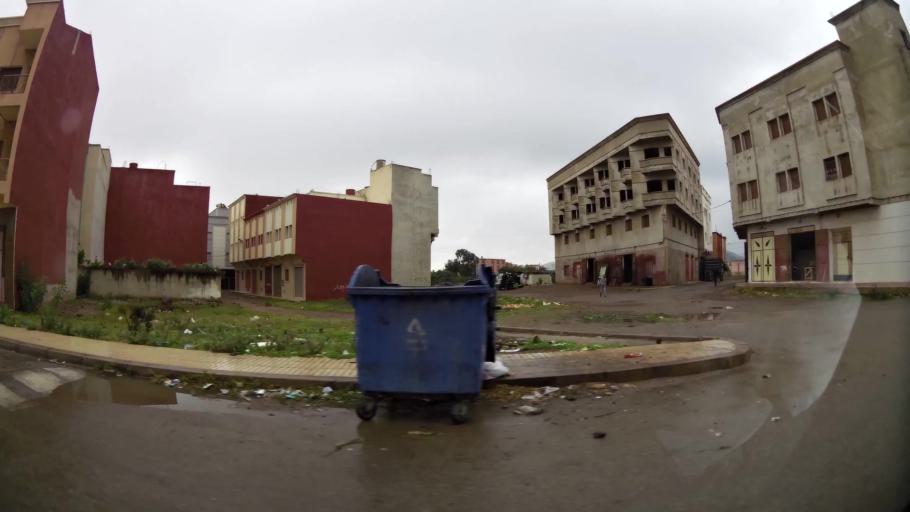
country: MA
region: Oriental
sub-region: Nador
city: Nador
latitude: 35.1615
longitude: -2.9642
